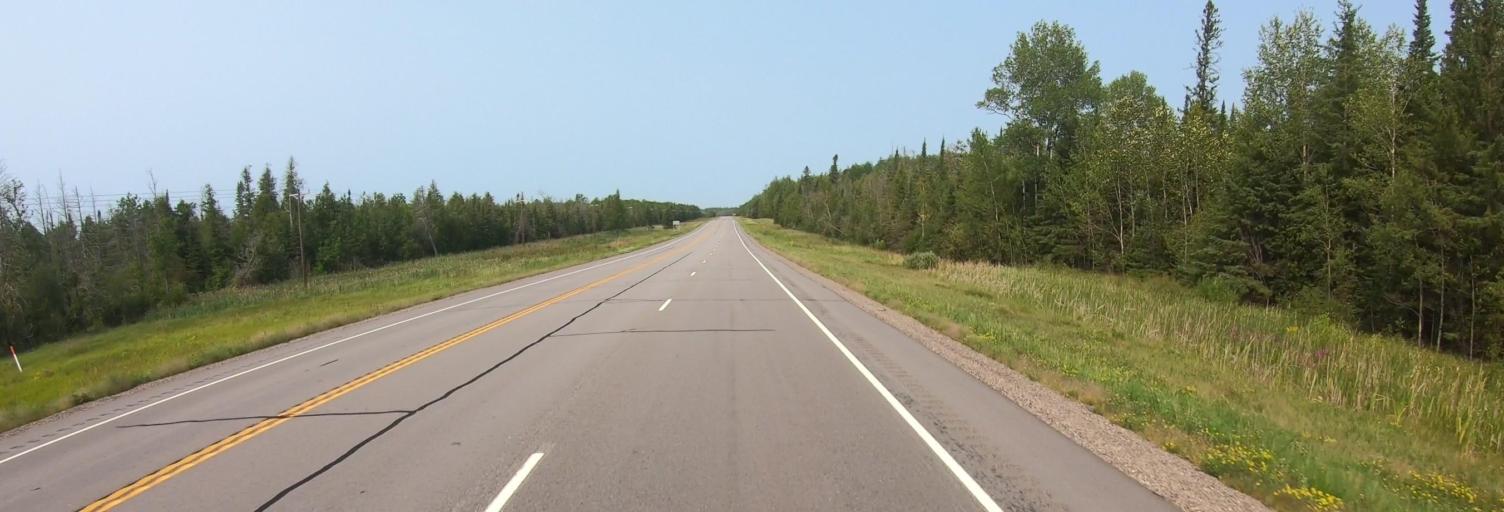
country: CA
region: Ontario
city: Fort Frances
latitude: 48.4027
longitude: -93.0248
